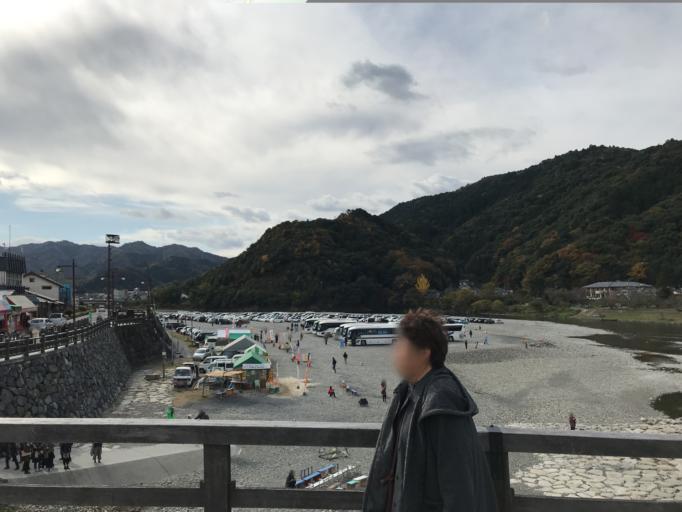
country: JP
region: Yamaguchi
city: Iwakuni
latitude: 34.1673
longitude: 132.1789
